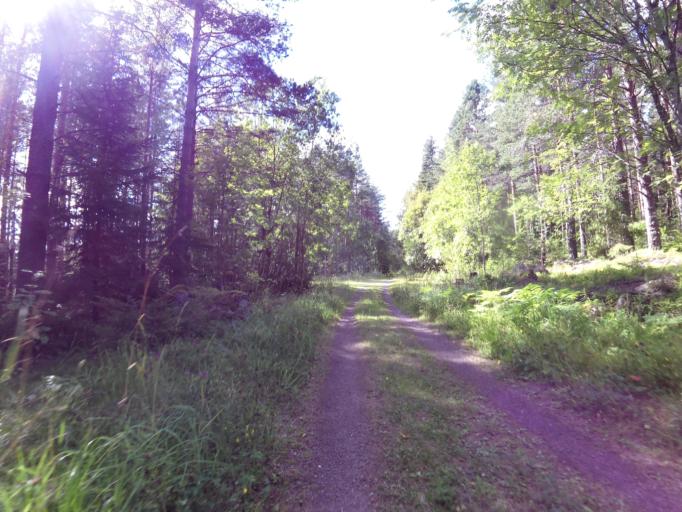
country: SE
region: Gaevleborg
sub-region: Hofors Kommun
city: Hofors
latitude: 60.5442
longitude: 16.2463
